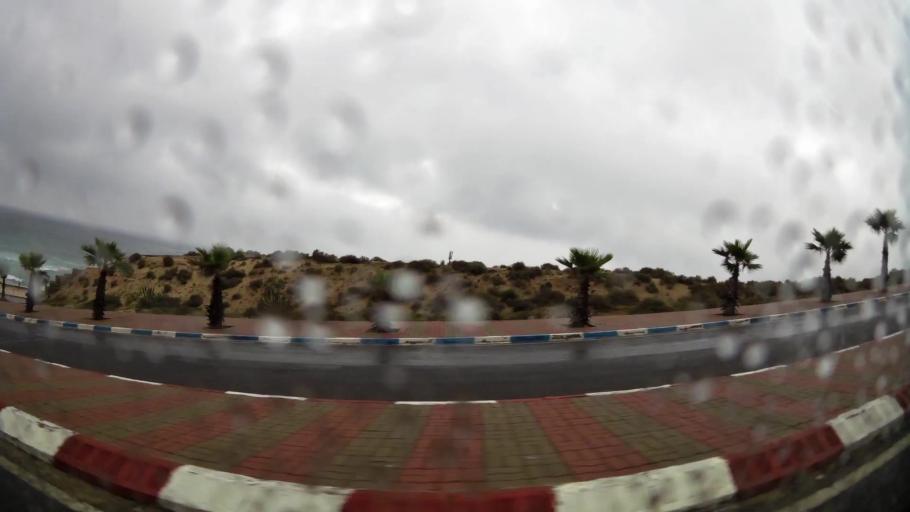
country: MA
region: Taza-Al Hoceima-Taounate
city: Tirhanimine
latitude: 35.2466
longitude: -3.9574
